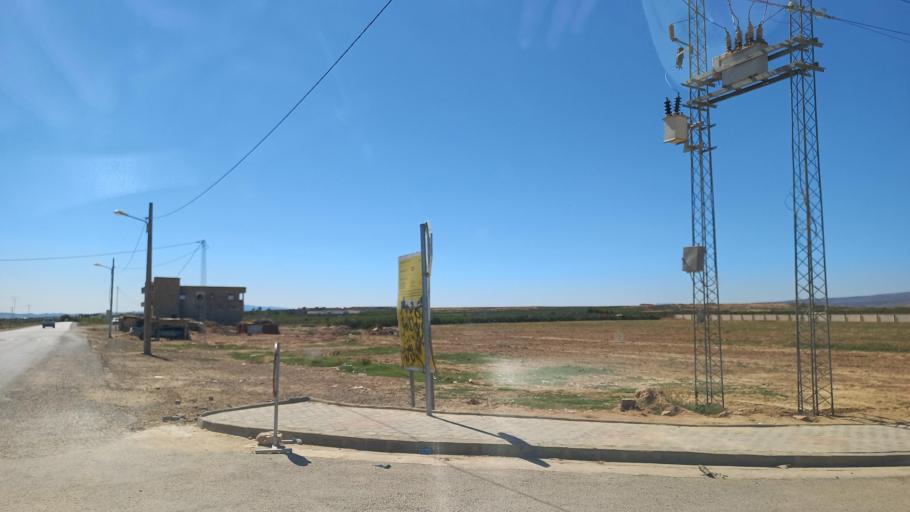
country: TN
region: Al Qasrayn
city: Sbiba
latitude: 35.3579
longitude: 9.0931
